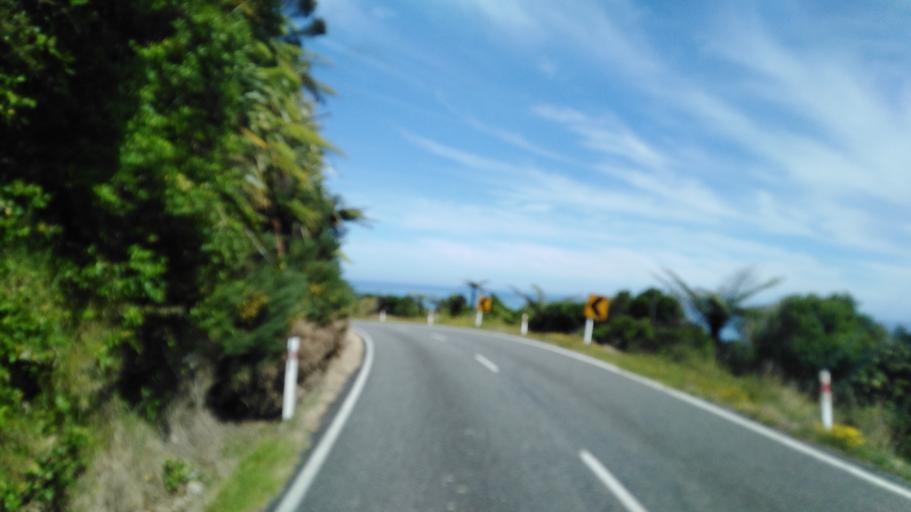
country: NZ
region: West Coast
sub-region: Buller District
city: Westport
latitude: -41.5727
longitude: 171.9046
